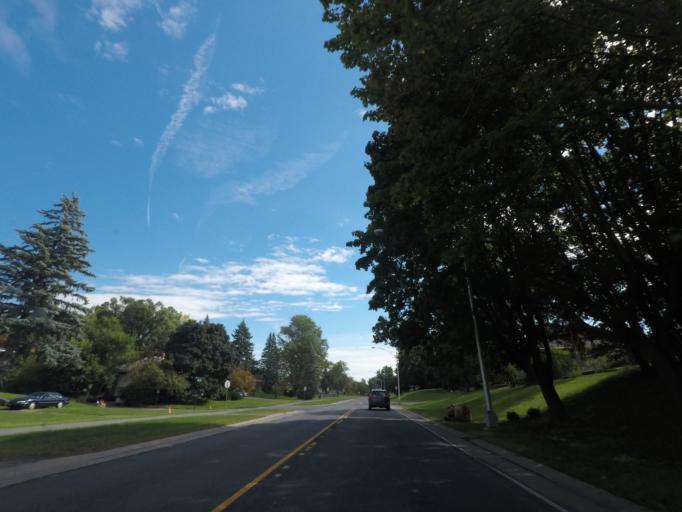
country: US
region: New York
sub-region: Albany County
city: Albany
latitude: 42.6476
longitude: -73.7929
